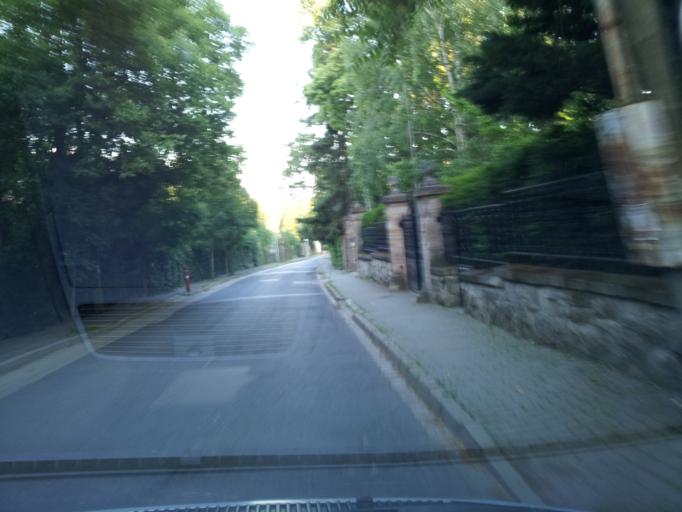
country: HU
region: Budapest
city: Budapest XII. keruelet
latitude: 47.5140
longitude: 18.9969
